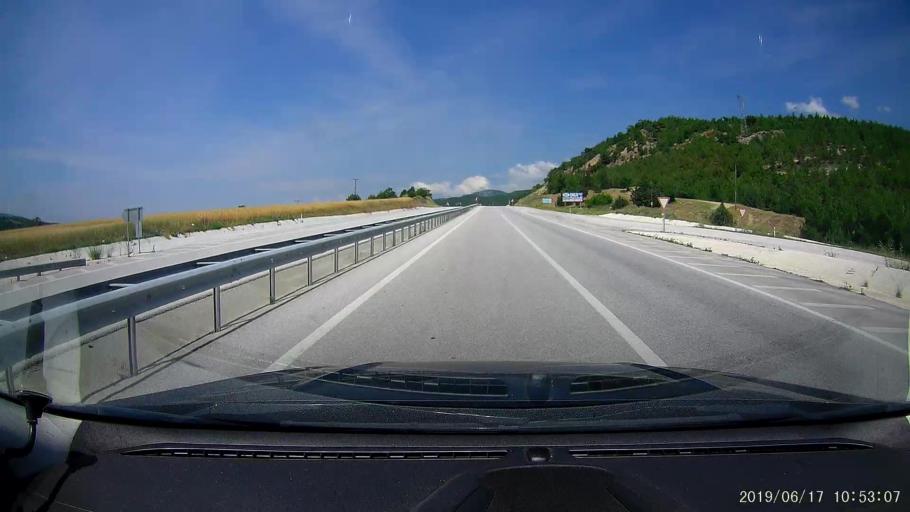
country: TR
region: Corum
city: Hacihamza
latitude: 41.0829
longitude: 34.3291
